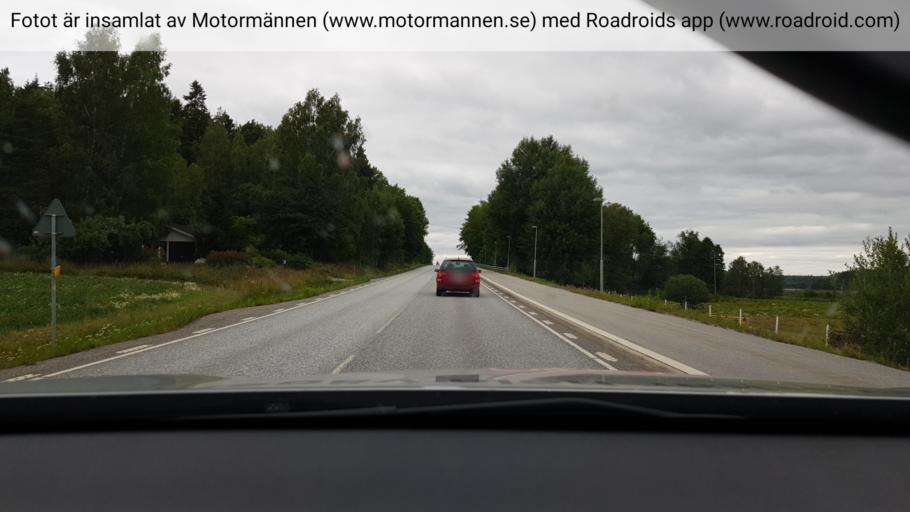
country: SE
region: Stockholm
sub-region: Nynashamns Kommun
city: Nynashamn
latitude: 58.9323
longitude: 17.9202
